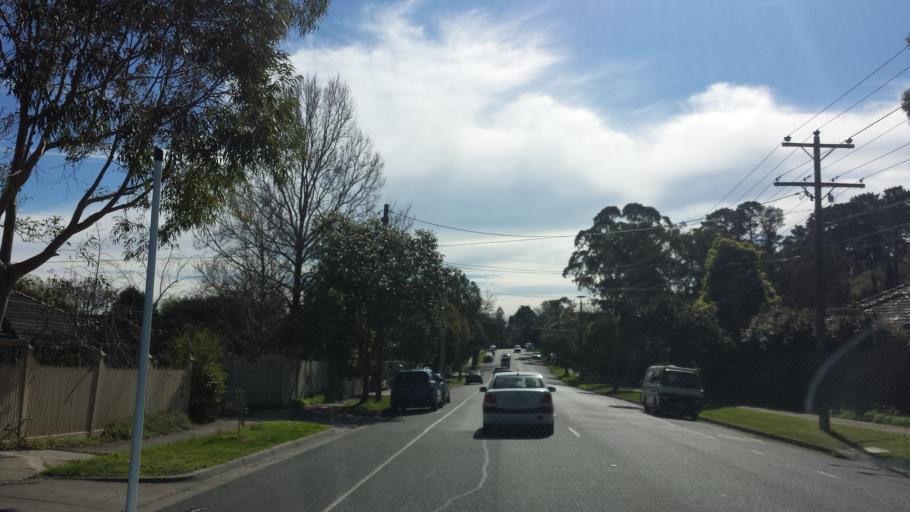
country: AU
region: Victoria
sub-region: Maroondah
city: Ringwood East
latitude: -37.8242
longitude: 145.2508
